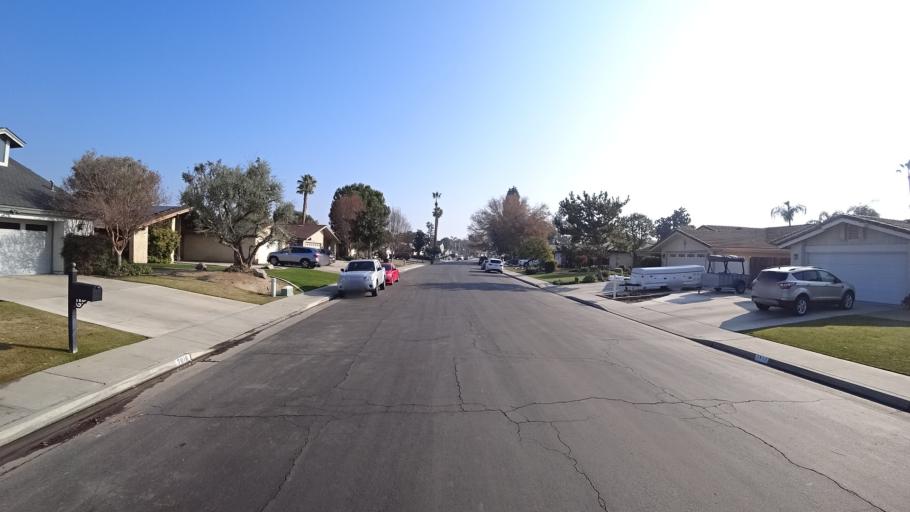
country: US
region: California
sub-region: Kern County
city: Greenacres
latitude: 35.3348
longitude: -119.0901
